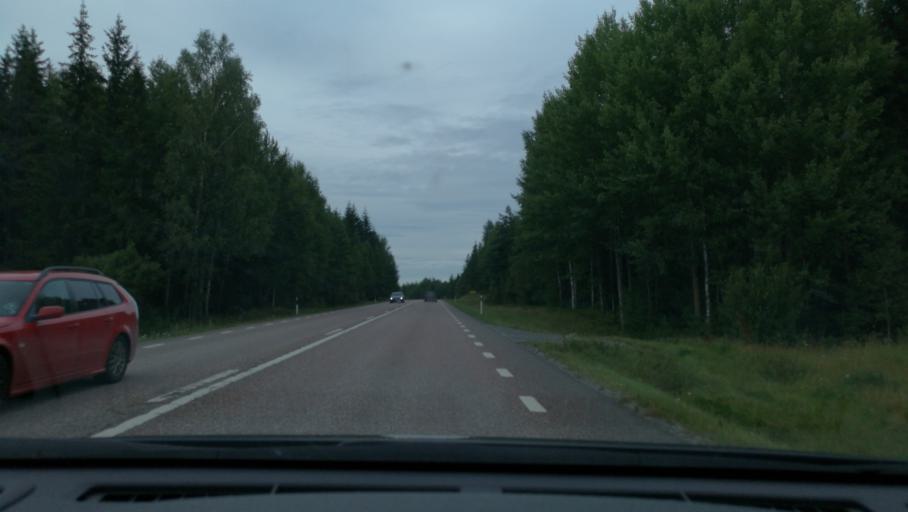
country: SE
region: Soedermanland
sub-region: Katrineholms Kommun
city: Katrineholm
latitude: 59.0567
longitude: 16.2230
